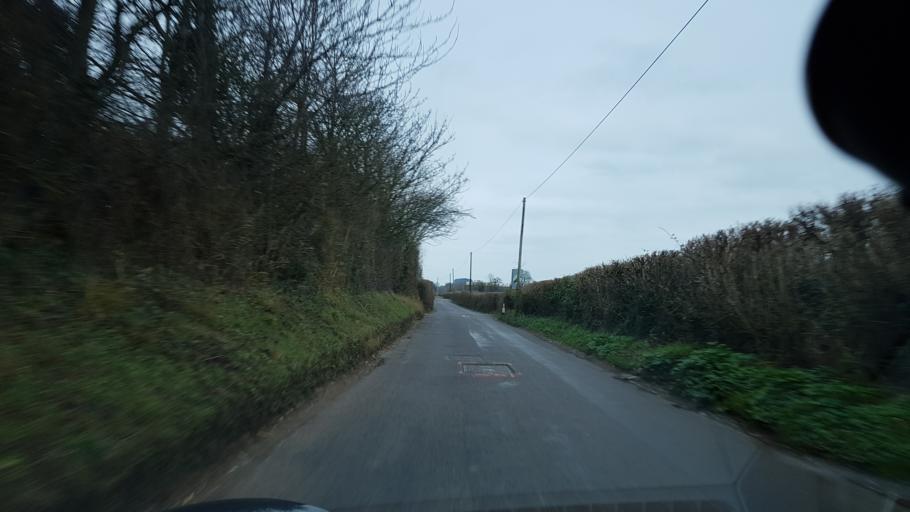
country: GB
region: England
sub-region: Somerset
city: Creech Saint Michael
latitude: 51.0066
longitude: -3.0591
